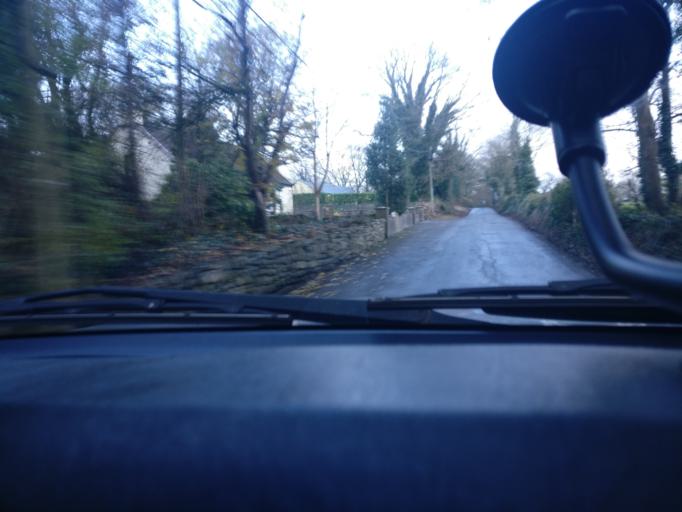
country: IE
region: Connaught
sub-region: County Galway
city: Athenry
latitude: 53.1986
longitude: -8.7039
